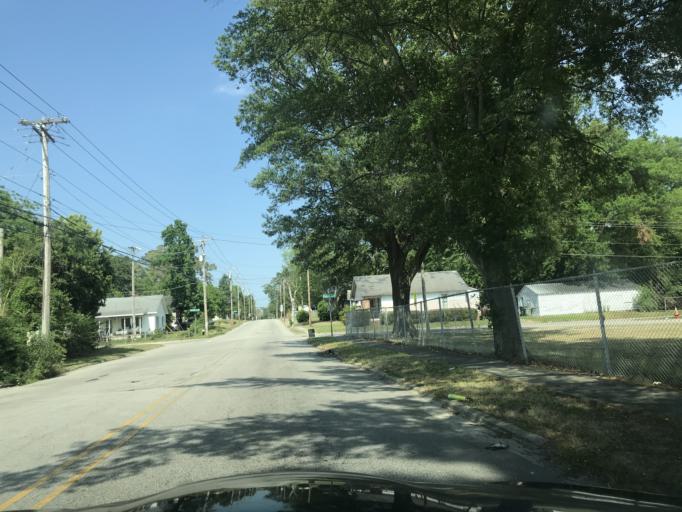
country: US
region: North Carolina
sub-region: Wilson County
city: Wilson
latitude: 35.7136
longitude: -77.9307
